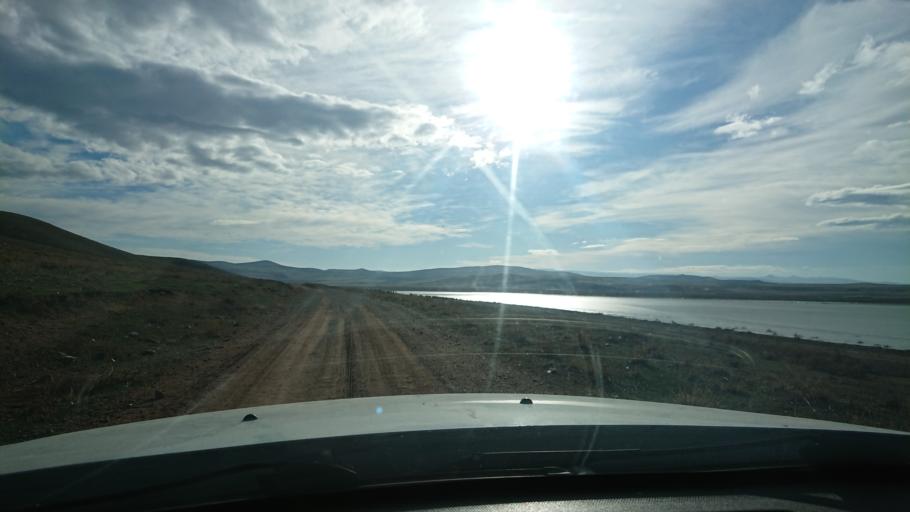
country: TR
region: Aksaray
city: Sariyahsi
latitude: 39.0474
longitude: 33.9727
